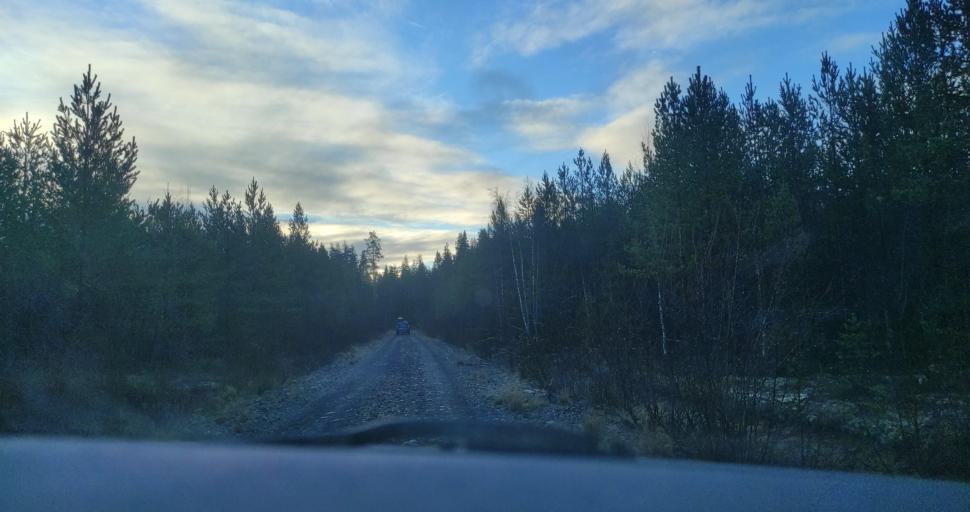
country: RU
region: Republic of Karelia
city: Pitkyaranta
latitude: 61.7366
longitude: 31.3645
